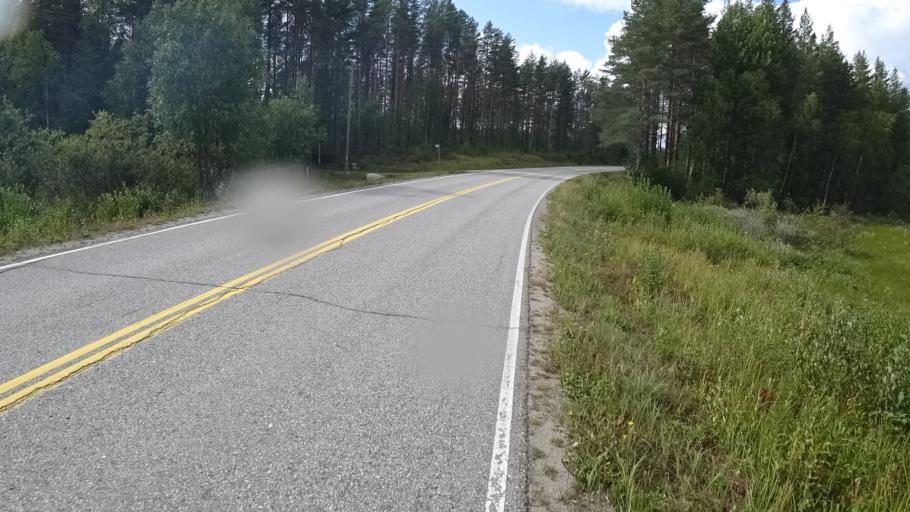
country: FI
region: North Karelia
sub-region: Joensuu
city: Ilomantsi
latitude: 62.6175
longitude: 31.2064
